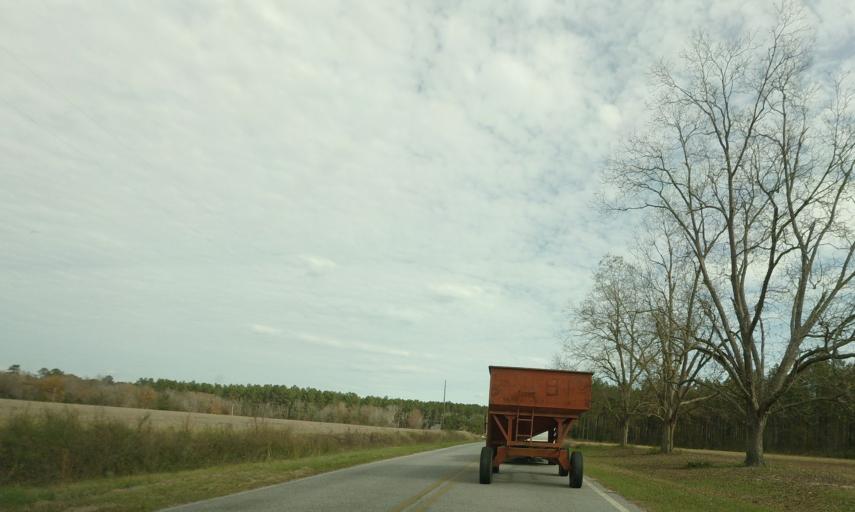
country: US
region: Georgia
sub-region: Dodge County
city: Chester
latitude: 32.4673
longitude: -83.1152
